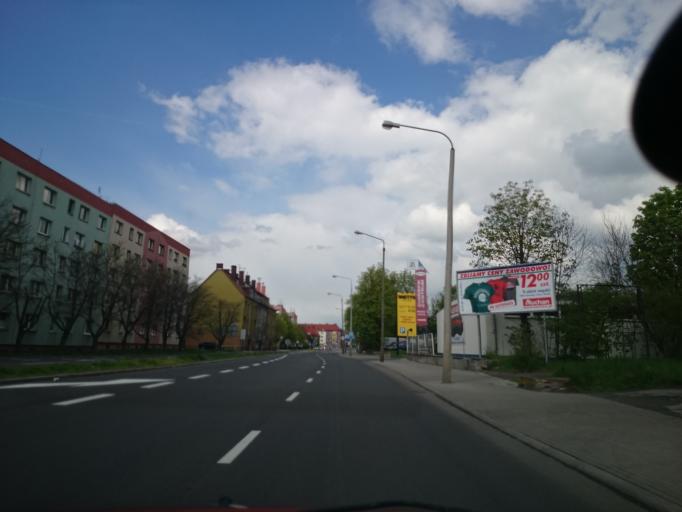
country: PL
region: Opole Voivodeship
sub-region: Powiat opolski
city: Opole
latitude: 50.6602
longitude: 17.9429
